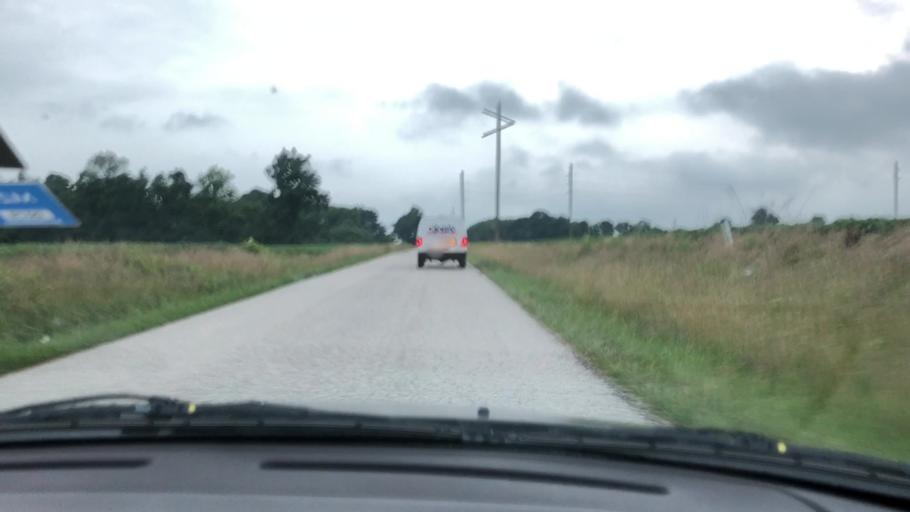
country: US
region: Indiana
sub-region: Greene County
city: Linton
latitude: 38.9771
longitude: -87.2982
